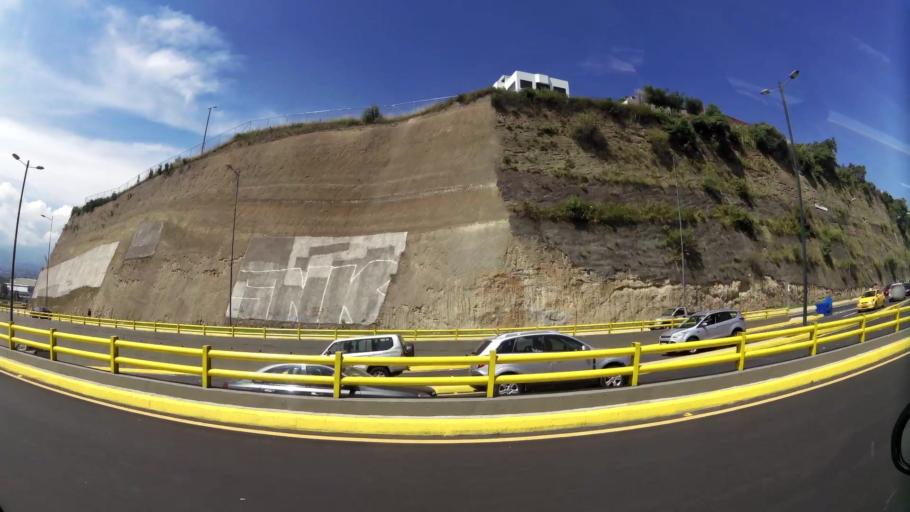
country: EC
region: Pichincha
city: Quito
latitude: -0.2051
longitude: -78.4318
